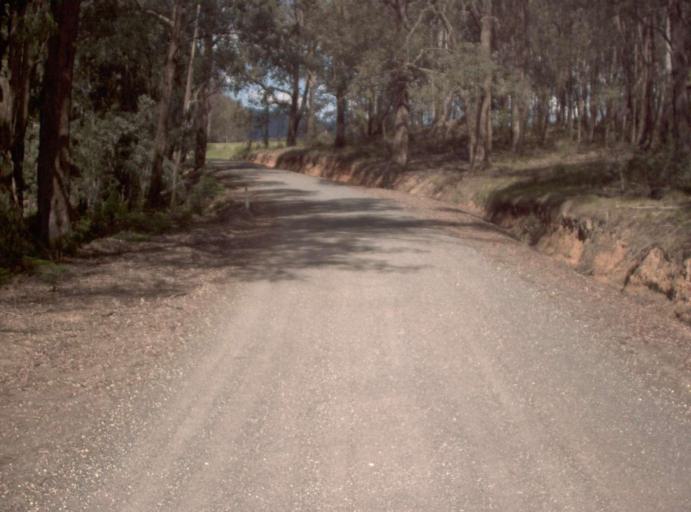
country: AU
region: New South Wales
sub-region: Bombala
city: Bombala
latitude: -37.1839
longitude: 148.7163
